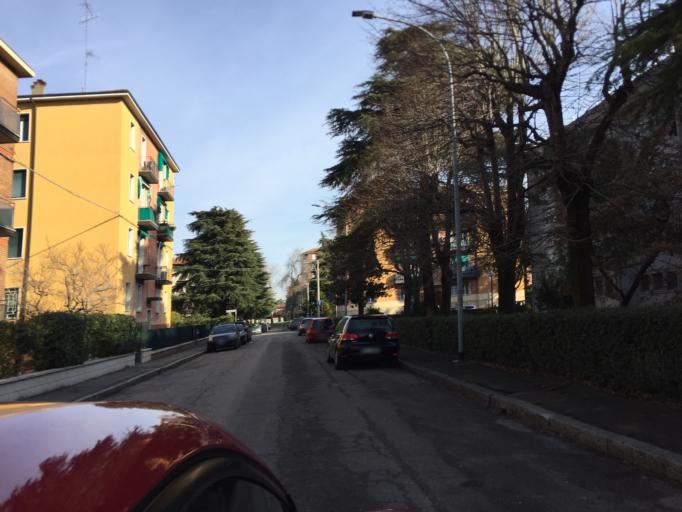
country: IT
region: Emilia-Romagna
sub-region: Provincia di Bologna
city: Casalecchio di Reno
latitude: 44.5009
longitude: 11.2985
